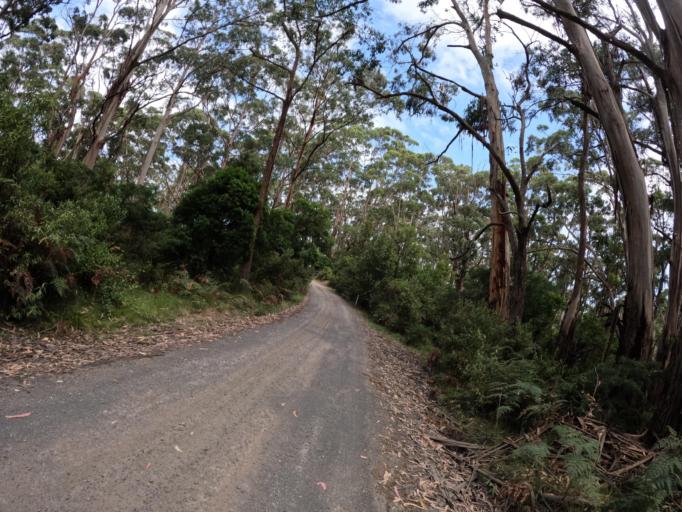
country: AU
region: Victoria
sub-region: Colac-Otway
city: Apollo Bay
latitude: -38.7895
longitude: 143.6190
